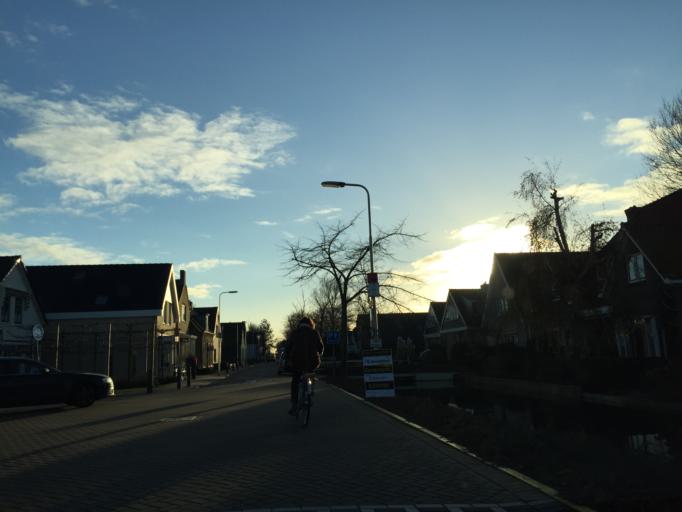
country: NL
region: South Holland
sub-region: Gemeente Lansingerland
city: Bleiswijk
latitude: 52.0139
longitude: 4.5316
